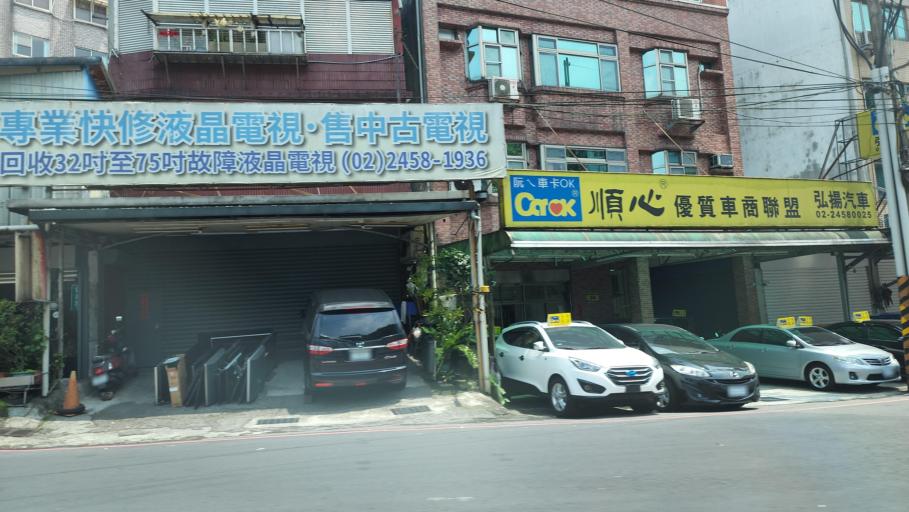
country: TW
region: Taiwan
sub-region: Keelung
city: Keelung
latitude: 25.1109
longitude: 121.7354
